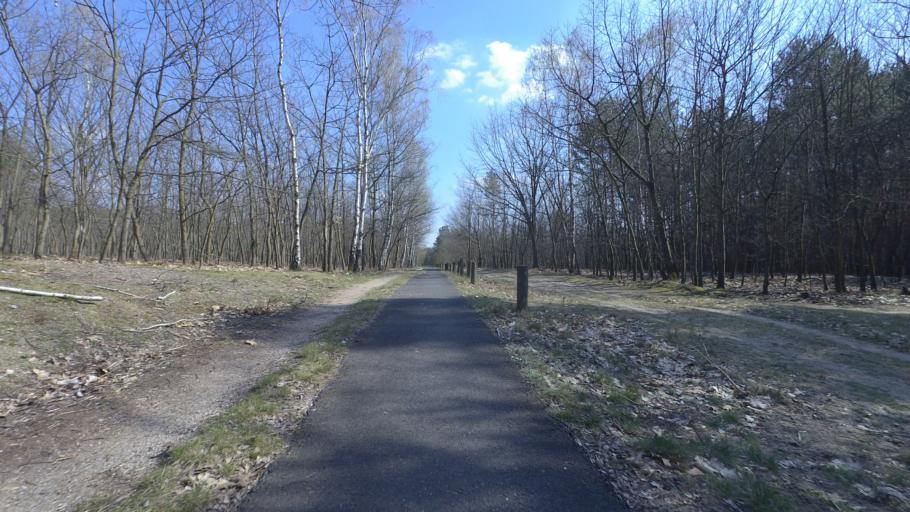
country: DE
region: Brandenburg
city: Mittenwalde
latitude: 52.1849
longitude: 13.5440
